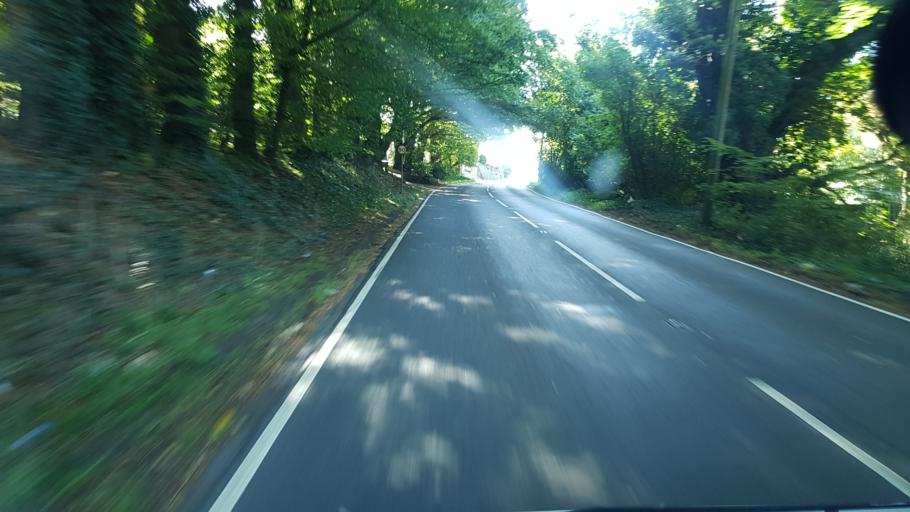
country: GB
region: England
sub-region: Kent
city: Borough Green
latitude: 51.2936
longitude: 0.3478
